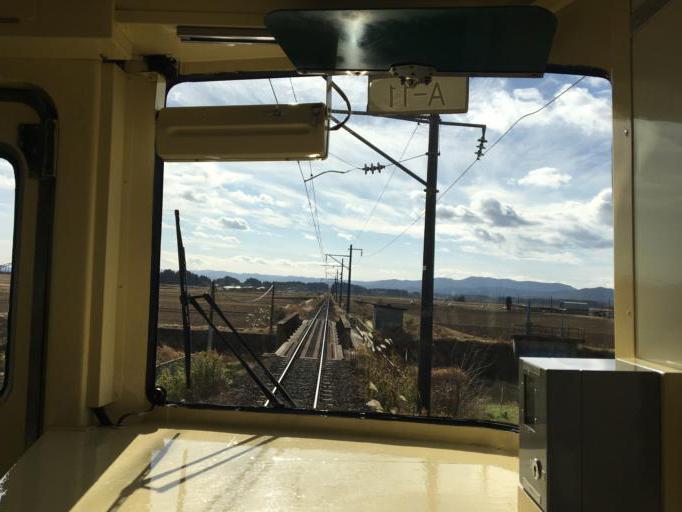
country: JP
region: Miyagi
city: Kakuda
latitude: 38.0157
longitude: 140.7799
